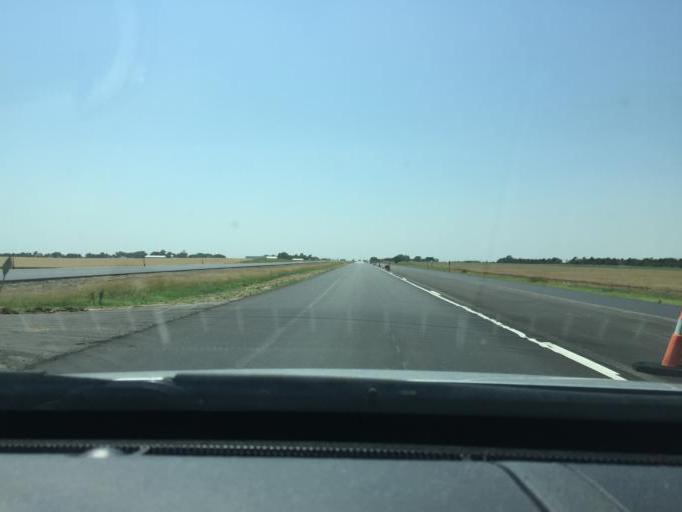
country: US
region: Kansas
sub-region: Reno County
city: South Hutchinson
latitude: 38.0136
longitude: -97.9799
